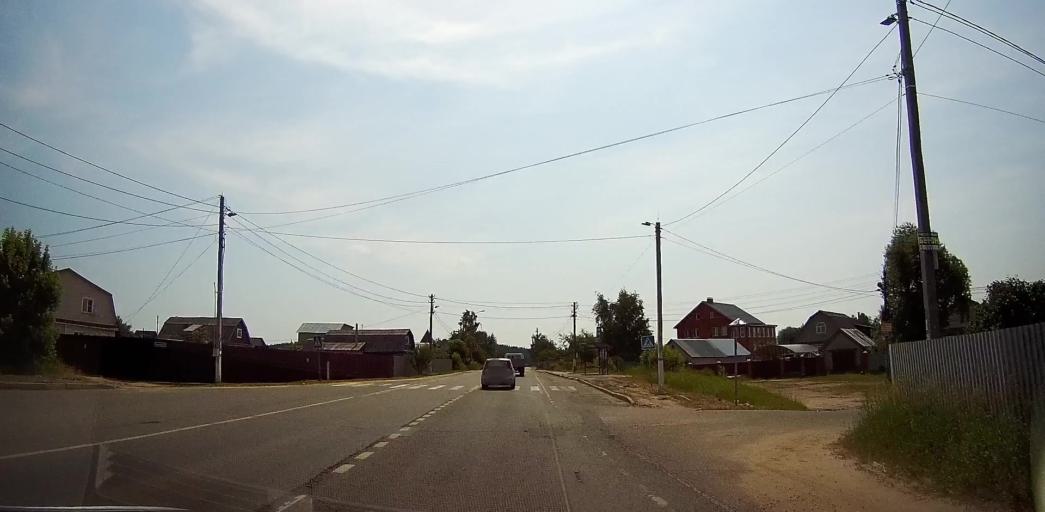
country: RU
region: Moskovskaya
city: Malyshevo
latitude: 55.5318
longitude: 38.3340
